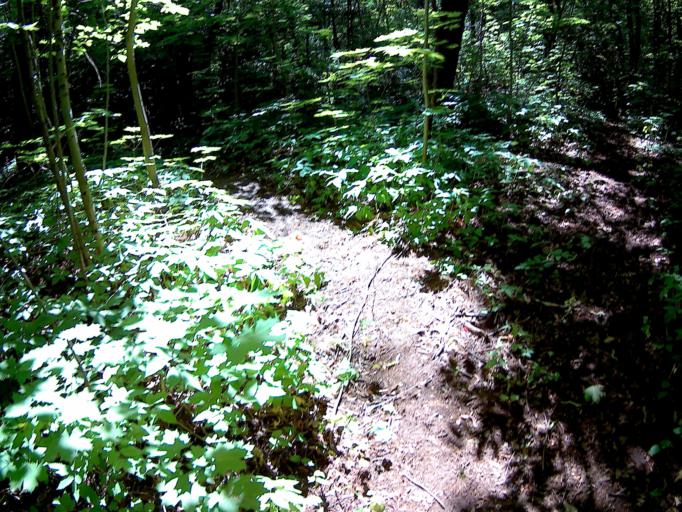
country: RU
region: Nizjnij Novgorod
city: Nizhniy Novgorod
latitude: 56.2271
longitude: 43.9222
